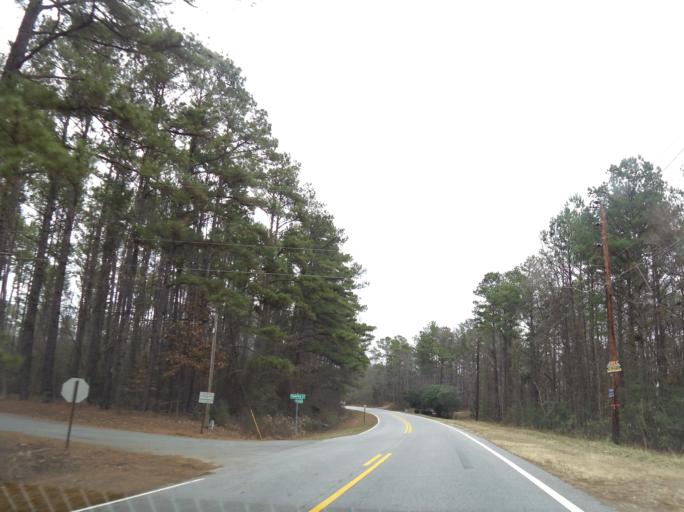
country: US
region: Georgia
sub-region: Bibb County
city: West Point
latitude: 32.8350
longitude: -83.8129
